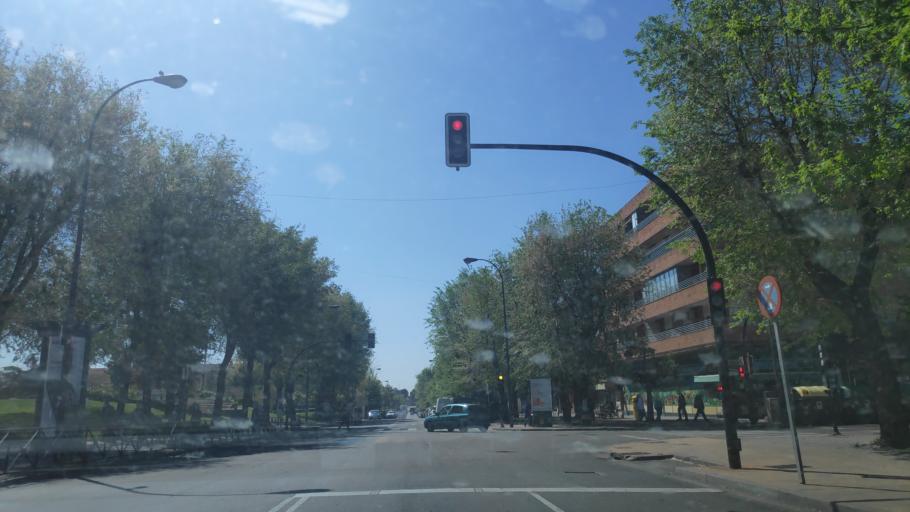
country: ES
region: Madrid
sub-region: Provincia de Madrid
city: Getafe
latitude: 40.3091
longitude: -3.7251
